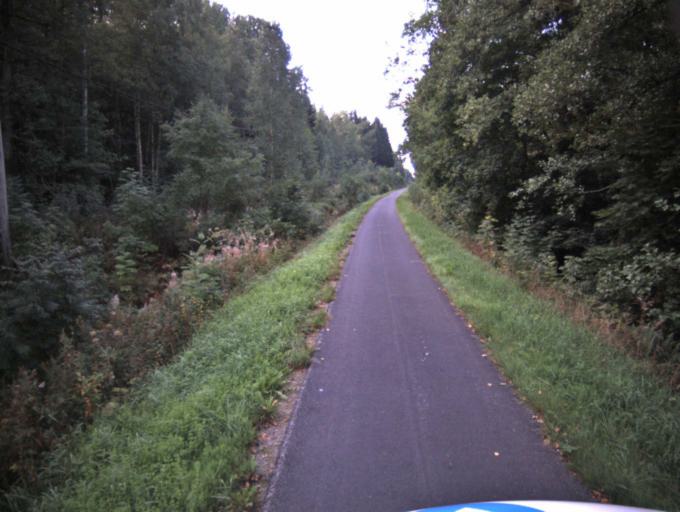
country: SE
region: Vaestra Goetaland
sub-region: Ulricehamns Kommun
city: Ulricehamn
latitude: 57.6964
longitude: 13.3922
